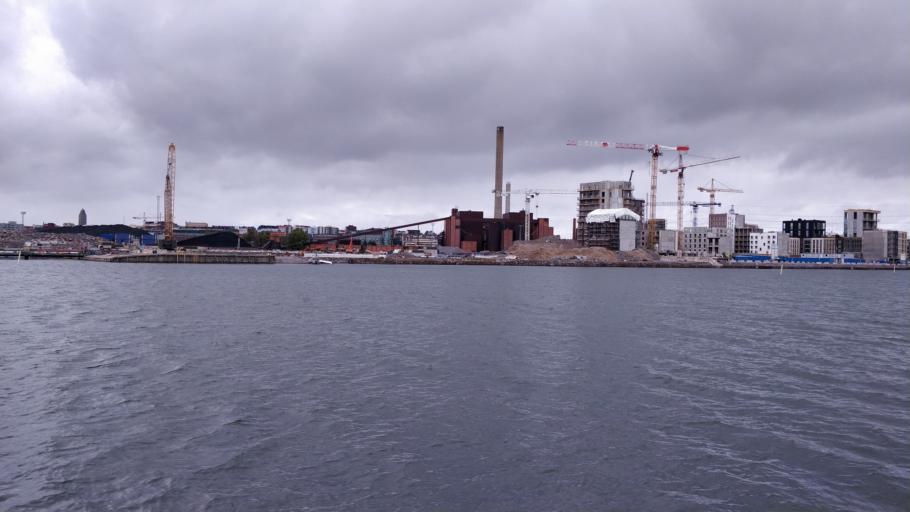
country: FI
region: Uusimaa
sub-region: Helsinki
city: Helsinki
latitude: 60.1776
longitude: 24.9808
